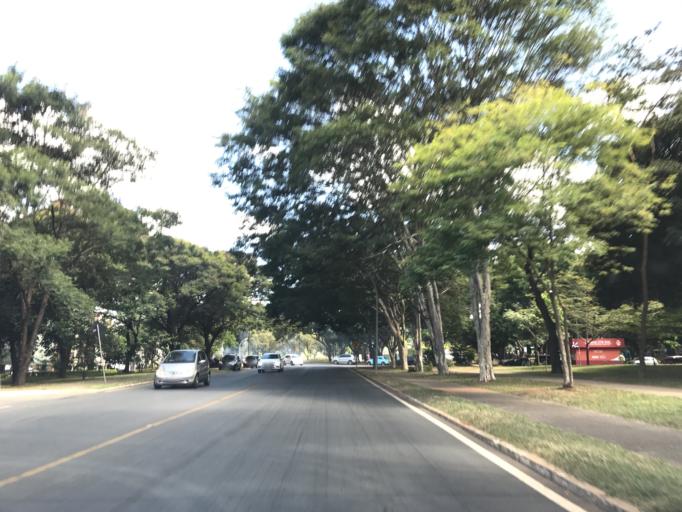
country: BR
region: Federal District
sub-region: Brasilia
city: Brasilia
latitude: -15.8346
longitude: -47.9193
